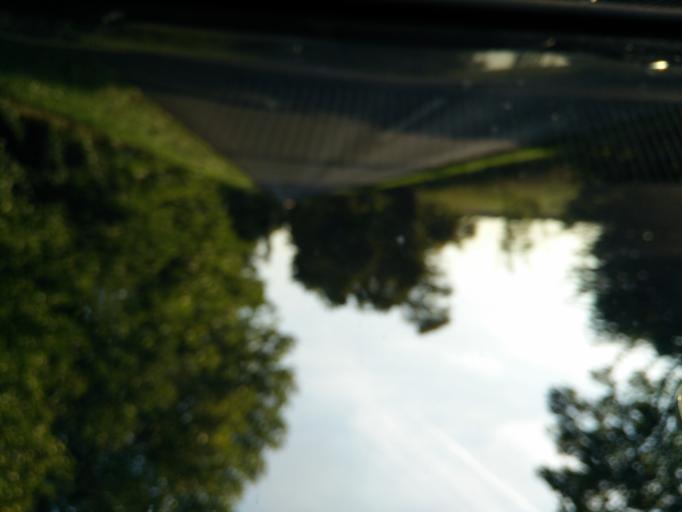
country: HU
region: Pest
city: Zsambek
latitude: 47.5252
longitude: 18.7409
